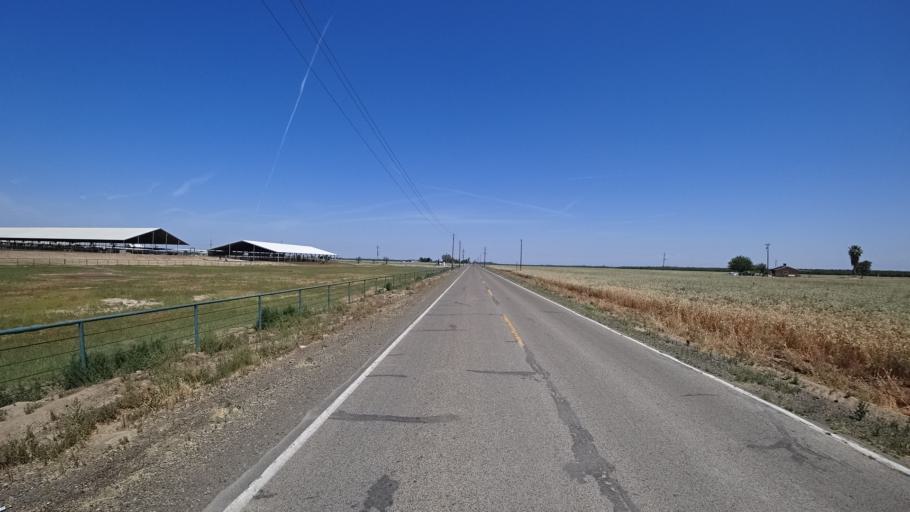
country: US
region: California
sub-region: Kings County
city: Armona
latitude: 36.2233
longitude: -119.7087
